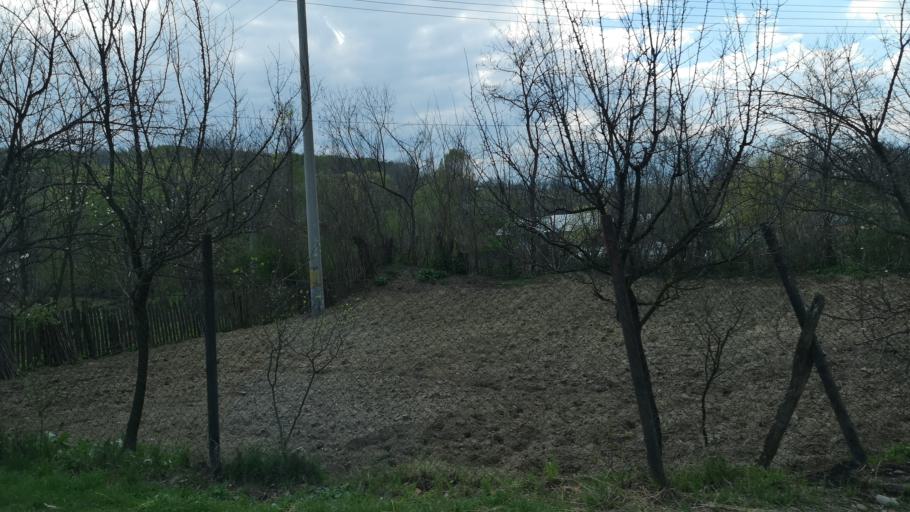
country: RO
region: Prahova
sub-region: Comuna Soimari
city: Soimari
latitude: 45.1728
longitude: 26.2111
